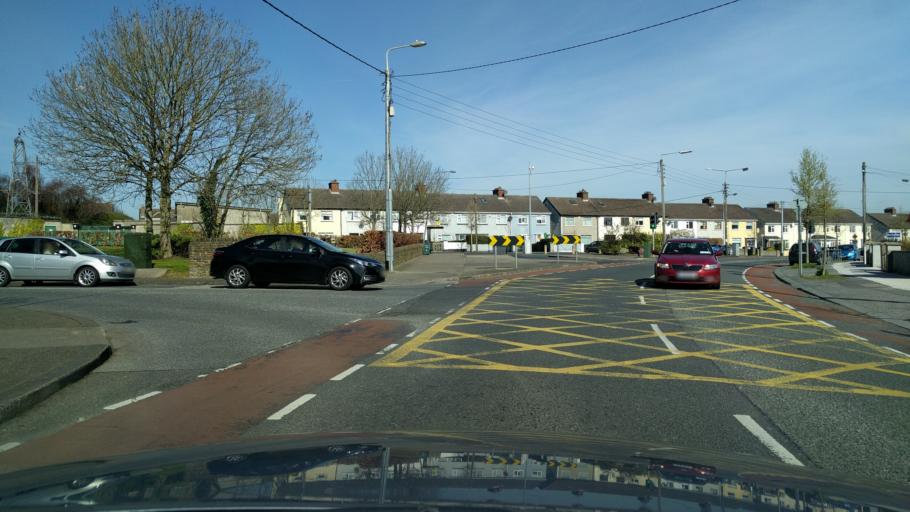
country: IE
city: Palmerstown
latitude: 53.3519
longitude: -6.3782
